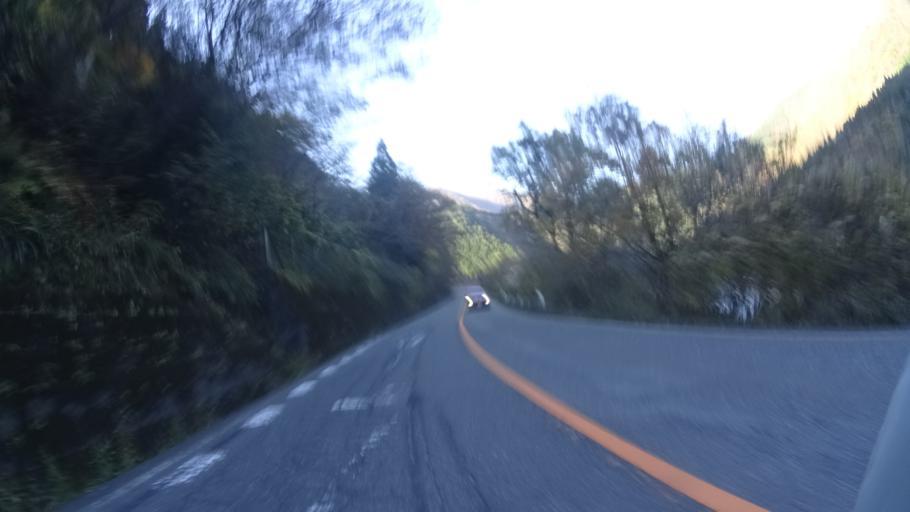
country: JP
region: Fukui
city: Ono
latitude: 35.9517
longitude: 136.6224
